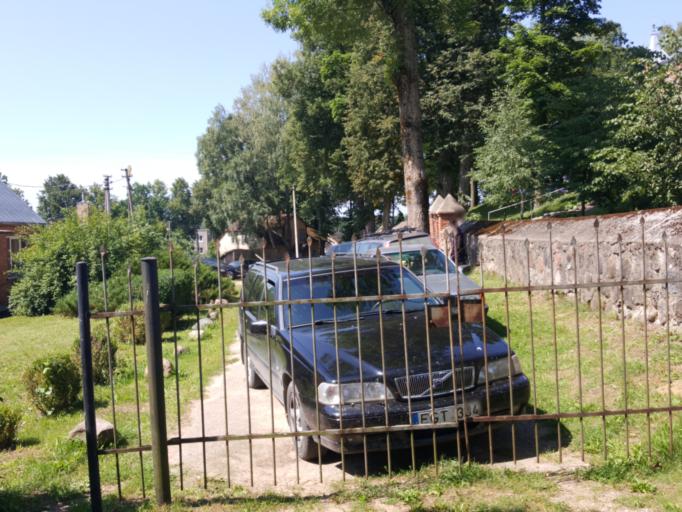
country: LT
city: Virbalis
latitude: 54.4682
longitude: 22.9237
